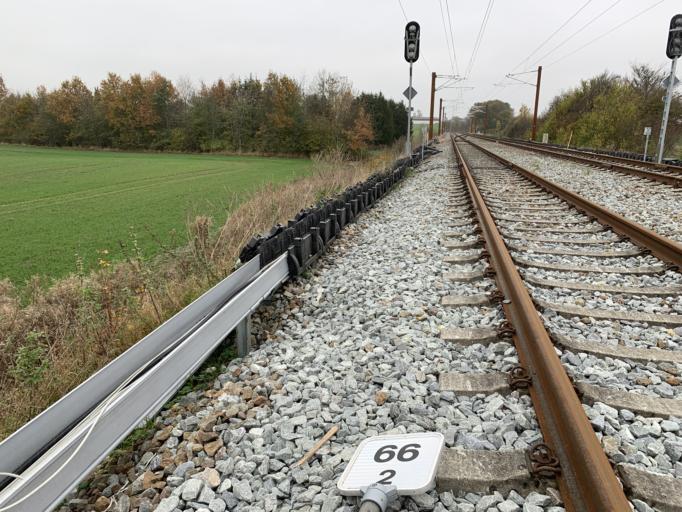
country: DK
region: Zealand
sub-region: Ringsted Kommune
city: Ringsted
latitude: 55.4276
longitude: 11.7596
